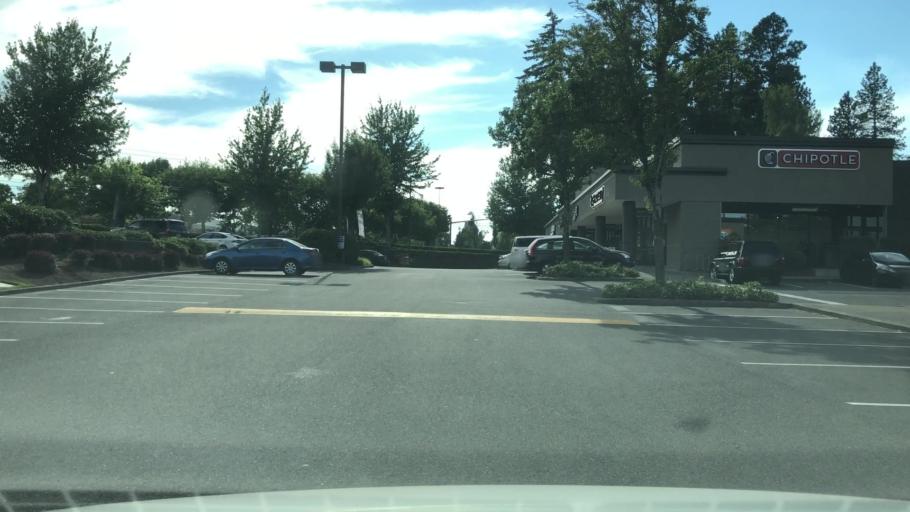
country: US
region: Oregon
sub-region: Washington County
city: Metzger
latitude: 45.4546
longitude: -122.7764
